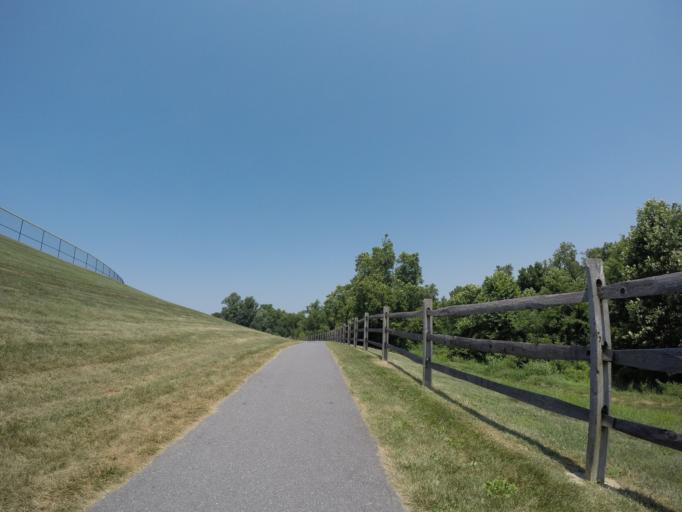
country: US
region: Maryland
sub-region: Frederick County
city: Urbana
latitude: 39.3389
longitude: -77.3635
